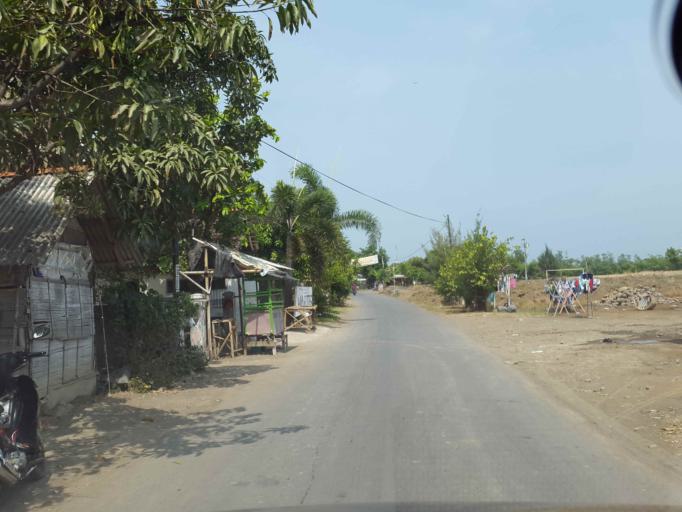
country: ID
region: Central Java
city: Dukuhturi
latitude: -6.8395
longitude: 109.0645
